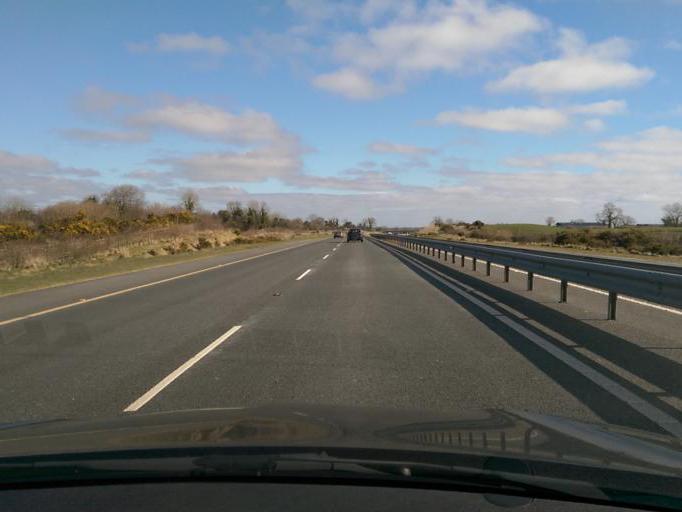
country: IE
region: Connaught
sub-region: County Galway
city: Ballinasloe
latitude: 53.3340
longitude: -8.1146
